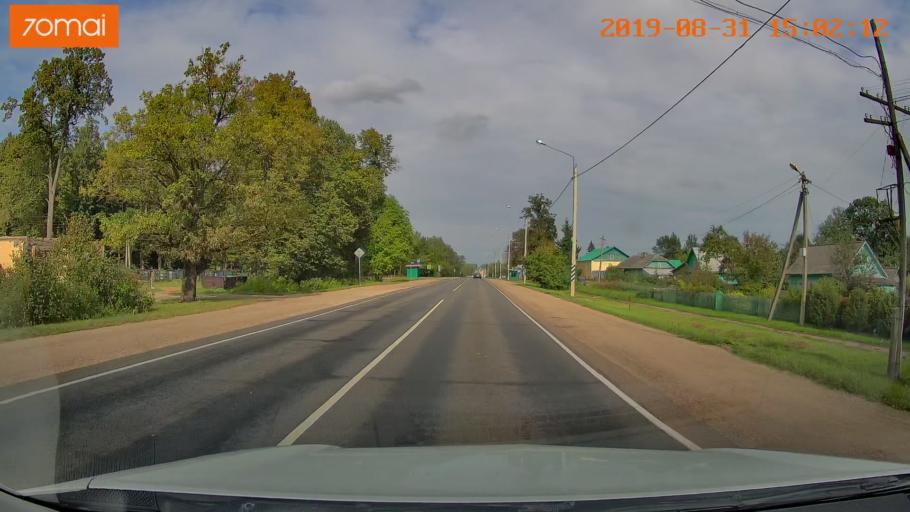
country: RU
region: Kaluga
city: Spas-Demensk
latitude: 54.3441
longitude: 34.0705
